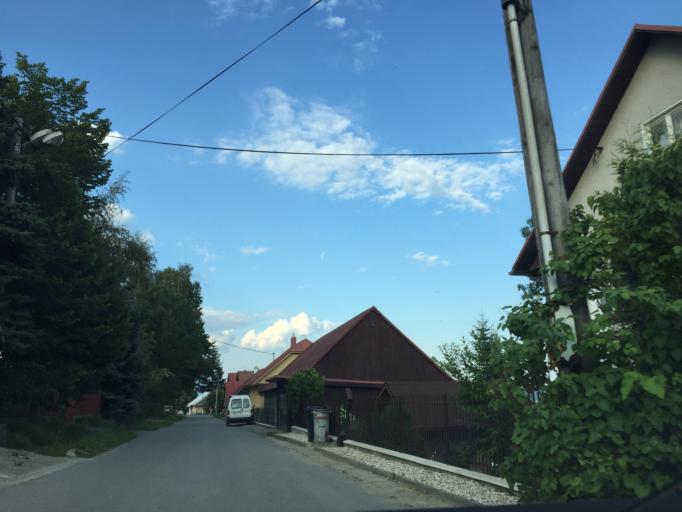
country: PL
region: Silesian Voivodeship
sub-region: Powiat zywiecki
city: Korbielow
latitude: 49.4590
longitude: 19.3222
